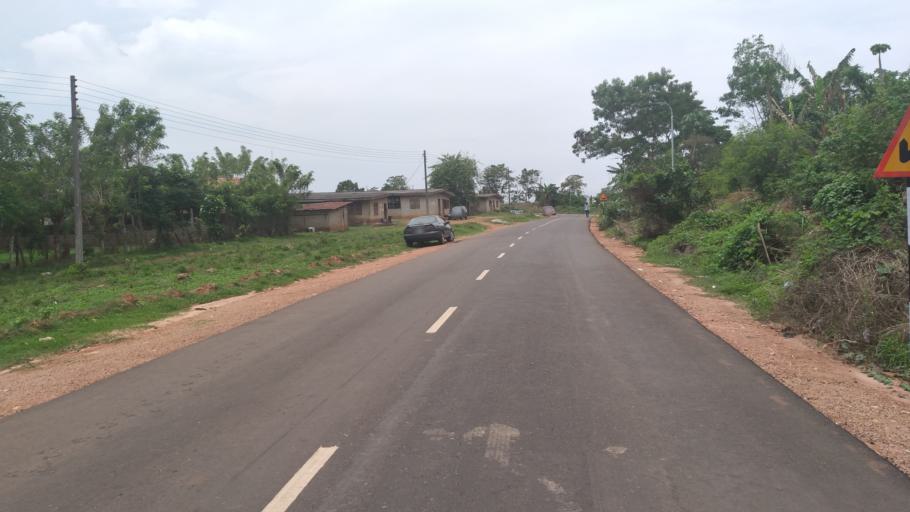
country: NG
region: Ondo
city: Ilare
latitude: 7.2997
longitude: 5.1451
